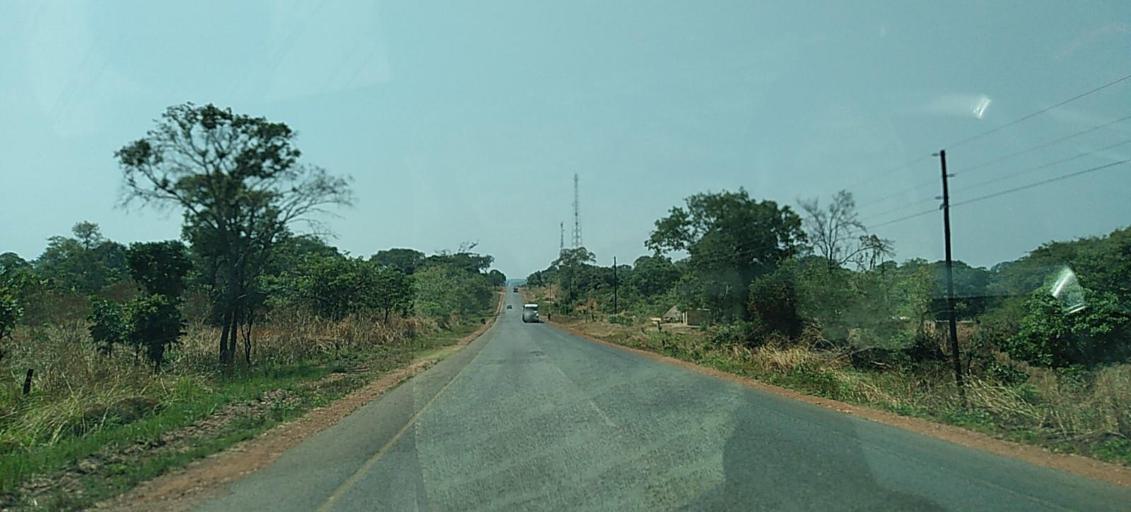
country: ZM
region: North-Western
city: Solwezi
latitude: -12.3269
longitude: 25.8849
